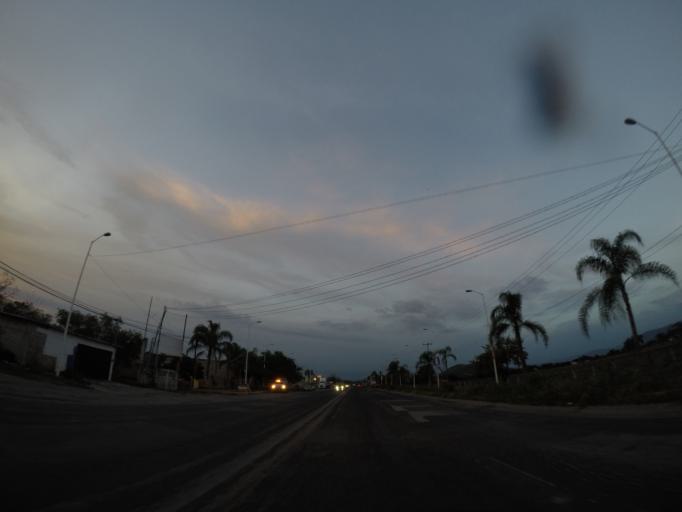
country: MX
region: Morelos
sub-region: Jojutla
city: Tehuixtla
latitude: 18.5925
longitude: -99.2587
